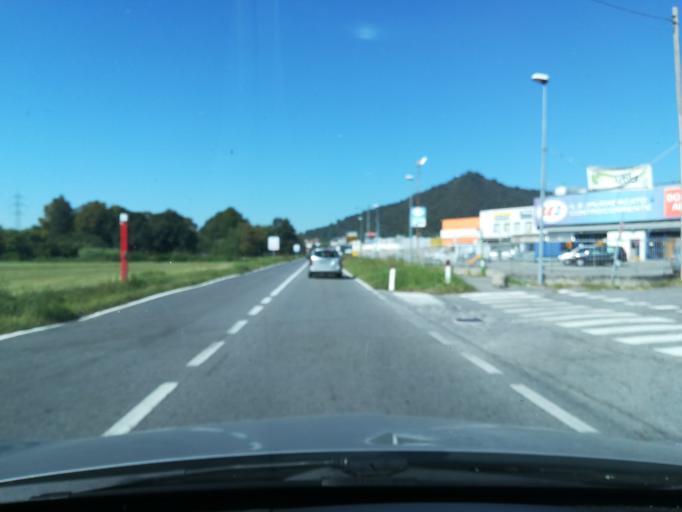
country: IT
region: Lombardy
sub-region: Provincia di Bergamo
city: San Paolo d'Argon
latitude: 45.6792
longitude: 9.7953
